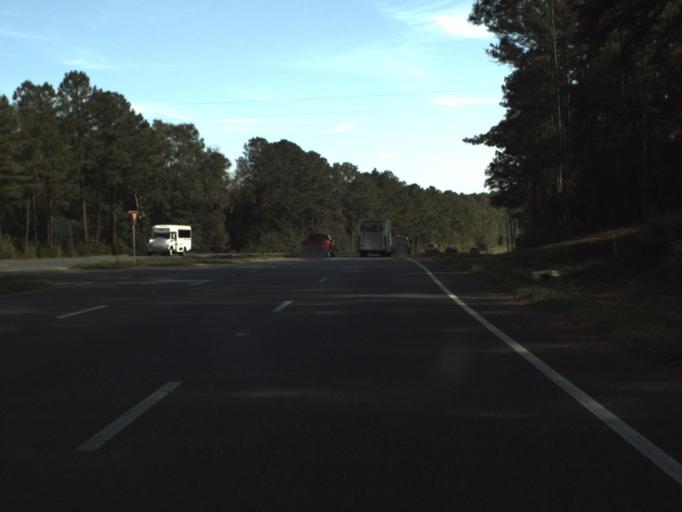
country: US
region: Florida
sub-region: Gadsden County
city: Midway
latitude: 30.5504
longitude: -84.4892
